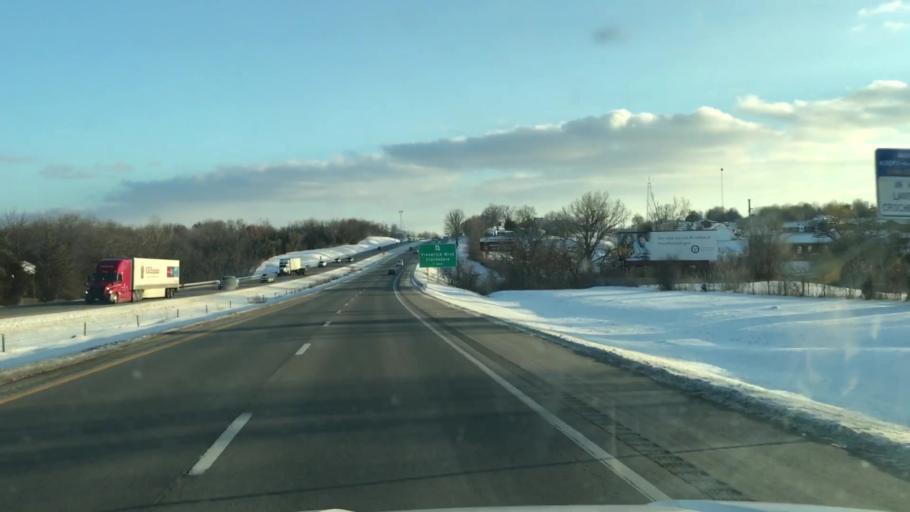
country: US
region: Missouri
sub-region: Andrew County
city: Country Club Village
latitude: 39.7917
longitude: -94.7963
